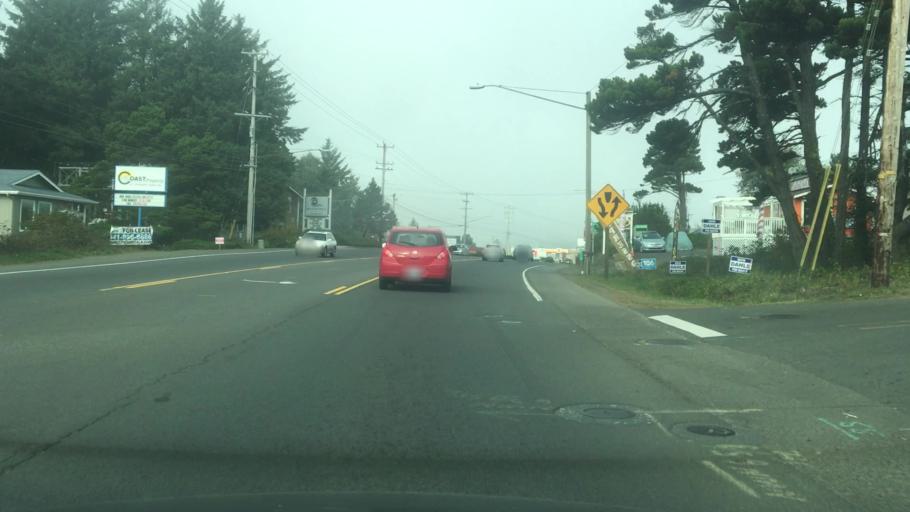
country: US
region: Oregon
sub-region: Lincoln County
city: Lincoln City
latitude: 44.9927
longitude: -124.0064
